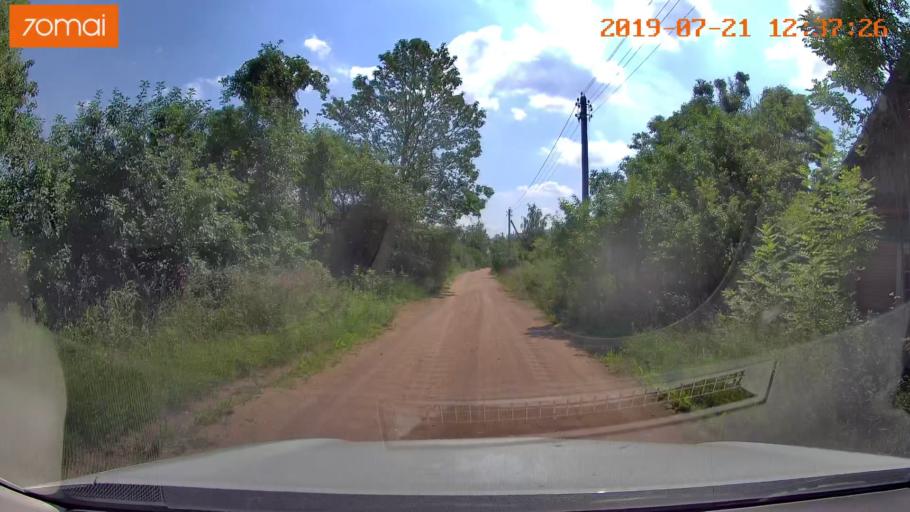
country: BY
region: Grodnenskaya
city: Lyubcha
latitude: 53.8640
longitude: 26.0060
